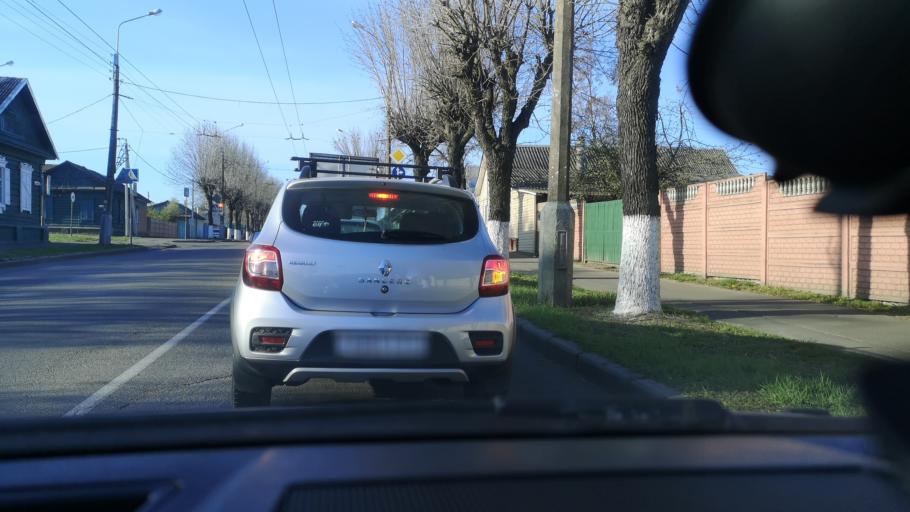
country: BY
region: Gomel
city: Gomel
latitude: 52.4297
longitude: 30.9750
